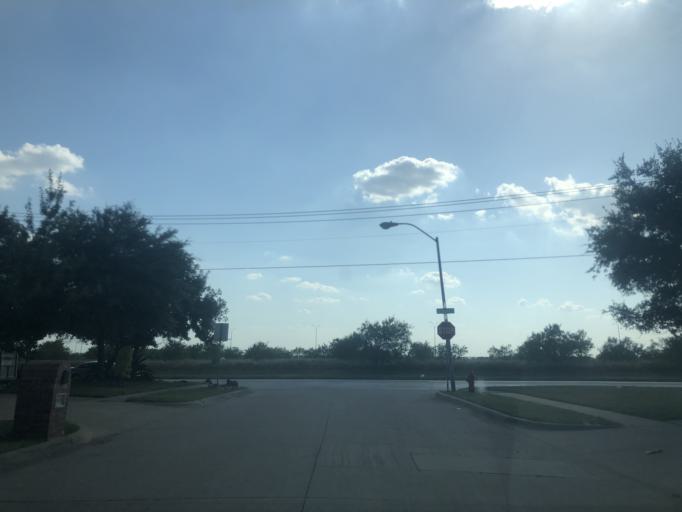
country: US
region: Texas
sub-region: Tarrant County
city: Saginaw
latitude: 32.8535
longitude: -97.3888
